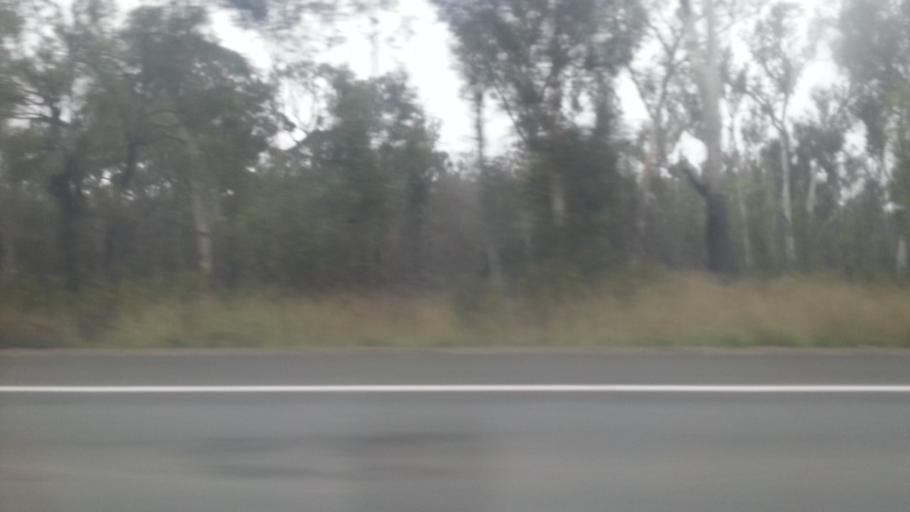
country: AU
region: New South Wales
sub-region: Penrith Municipality
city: Werrington Downs
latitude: -33.6829
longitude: 150.7393
